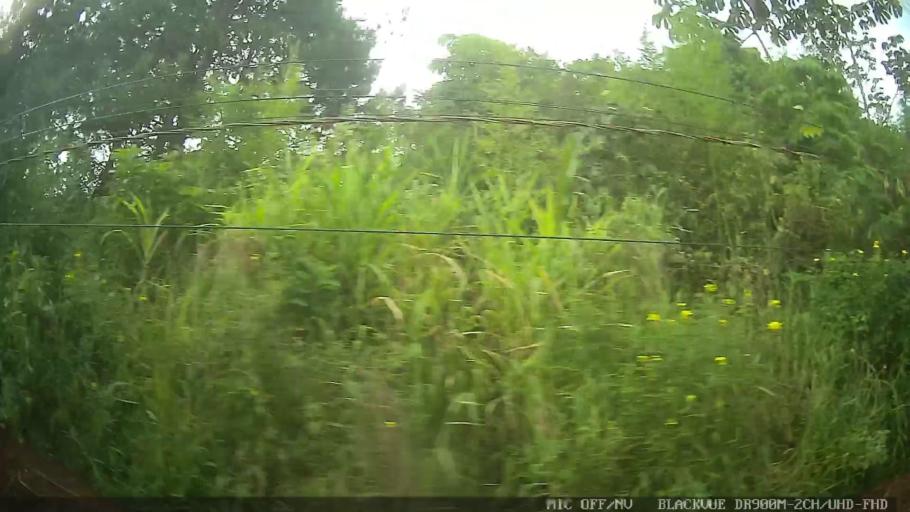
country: BR
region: Sao Paulo
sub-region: Suzano
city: Suzano
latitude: -23.5633
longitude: -46.3071
